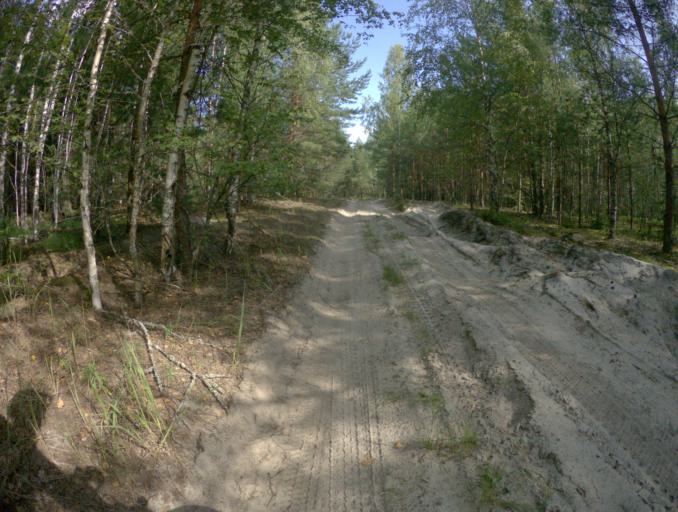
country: RU
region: Vladimir
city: Vorsha
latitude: 55.9096
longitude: 40.1625
